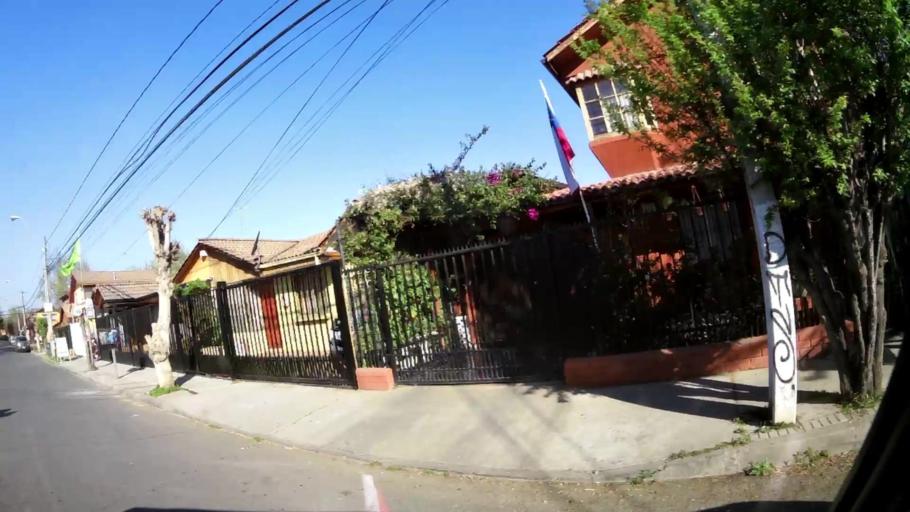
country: CL
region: Santiago Metropolitan
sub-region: Provincia de Santiago
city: Lo Prado
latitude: -33.4925
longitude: -70.7704
